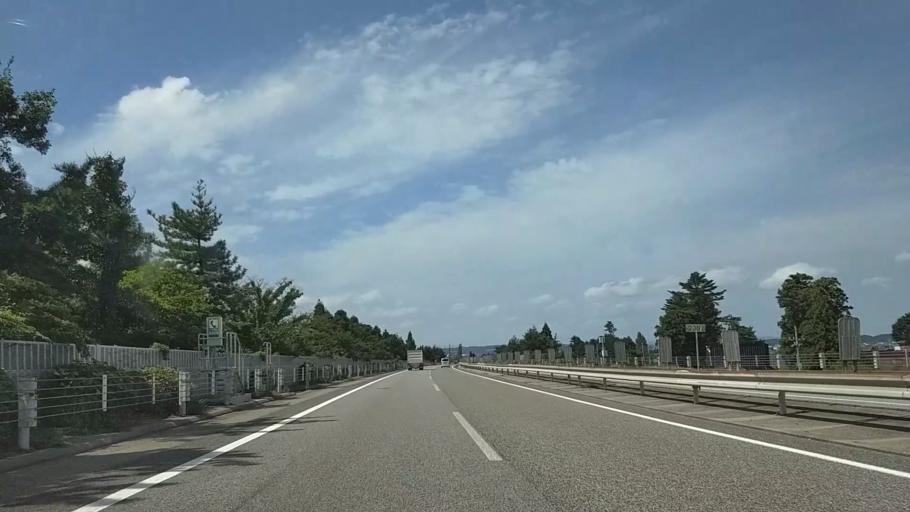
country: JP
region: Toyama
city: Toyama-shi
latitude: 36.6462
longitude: 137.2340
